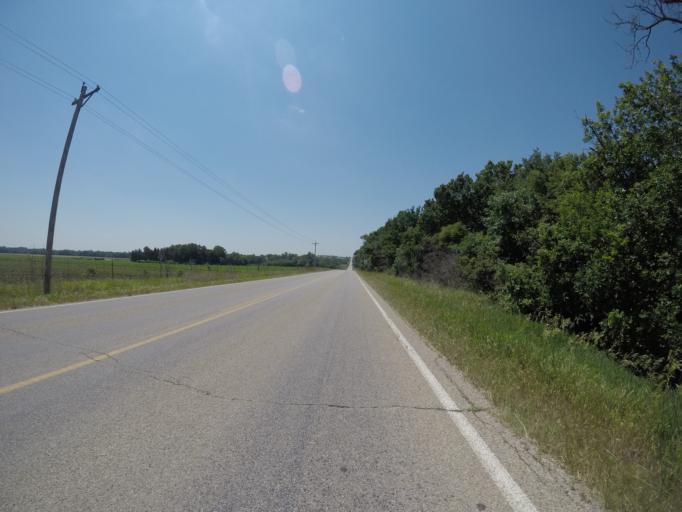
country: US
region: Kansas
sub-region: Pottawatomie County
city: Westmoreland
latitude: 39.2812
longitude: -96.4451
